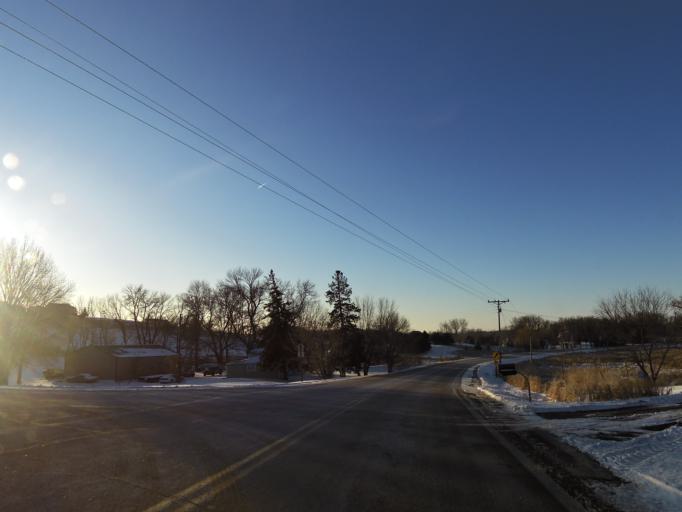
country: US
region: Minnesota
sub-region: Scott County
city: Prior Lake
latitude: 44.6596
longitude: -93.4602
